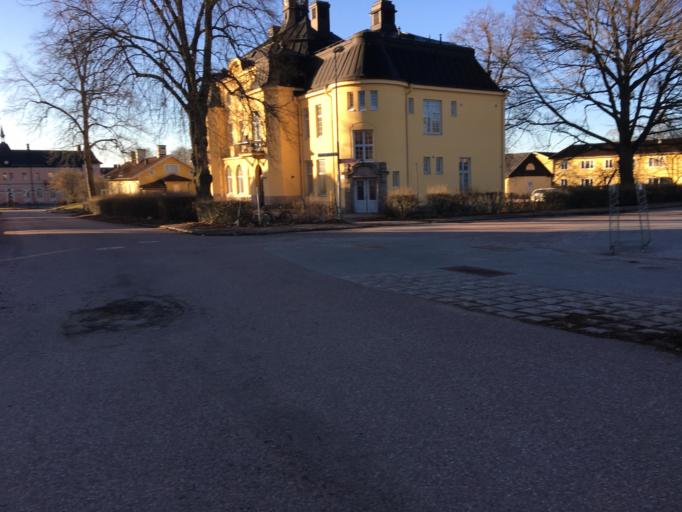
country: SE
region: Gaevleborg
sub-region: Sandvikens Kommun
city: Jarbo
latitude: 60.5832
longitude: 16.5321
